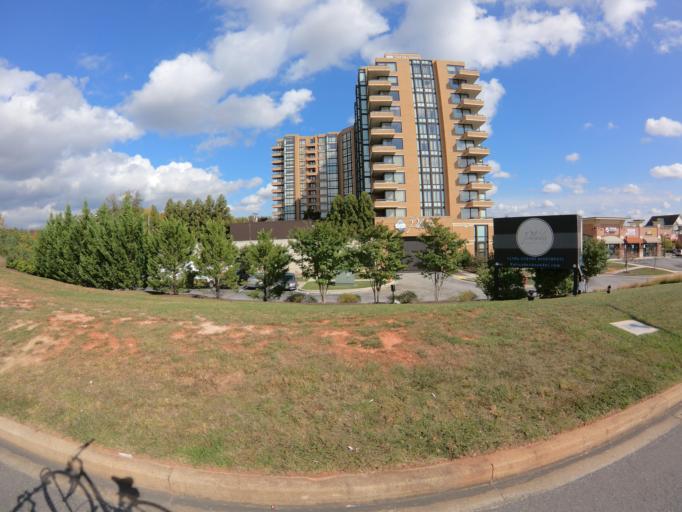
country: US
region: Maryland
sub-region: Anne Arundel County
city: Jessup
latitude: 39.1554
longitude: -76.7439
